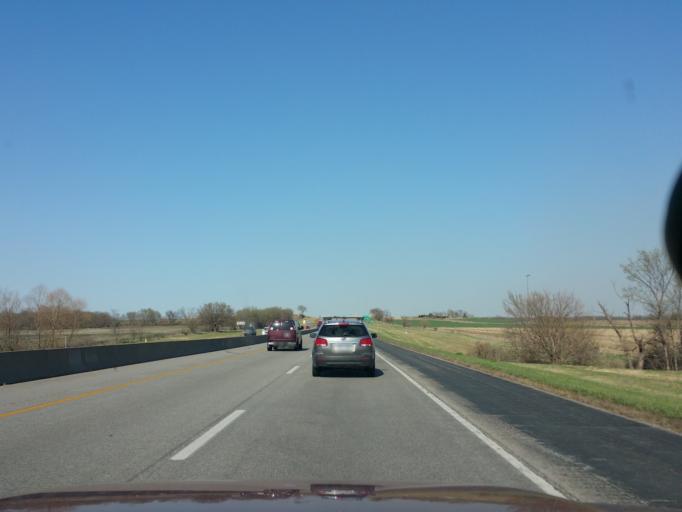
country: US
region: Kansas
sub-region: Leavenworth County
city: Tonganoxie
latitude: 39.0360
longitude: -95.1071
